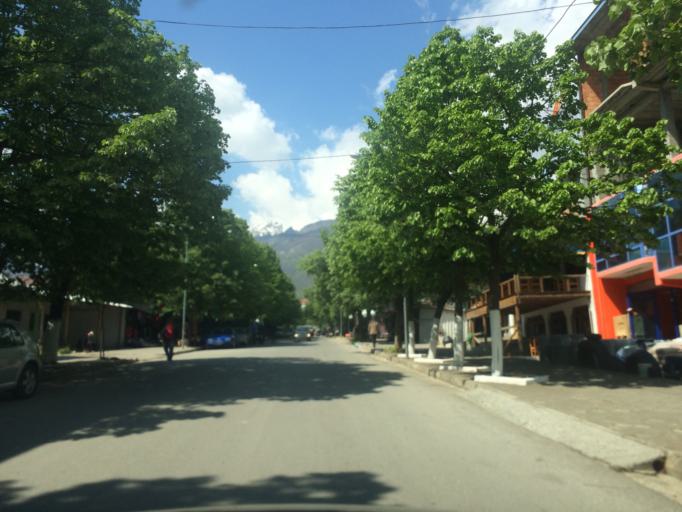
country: AL
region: Kukes
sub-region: Rrethi i Tropojes
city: Bajram Curri
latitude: 42.3571
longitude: 20.0791
